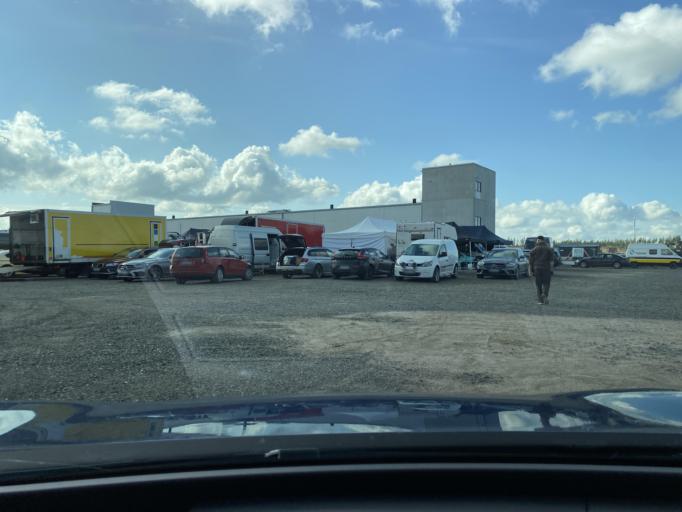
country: FI
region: Kymenlaakso
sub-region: Kouvola
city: Iitti
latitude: 60.8835
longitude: 26.4844
